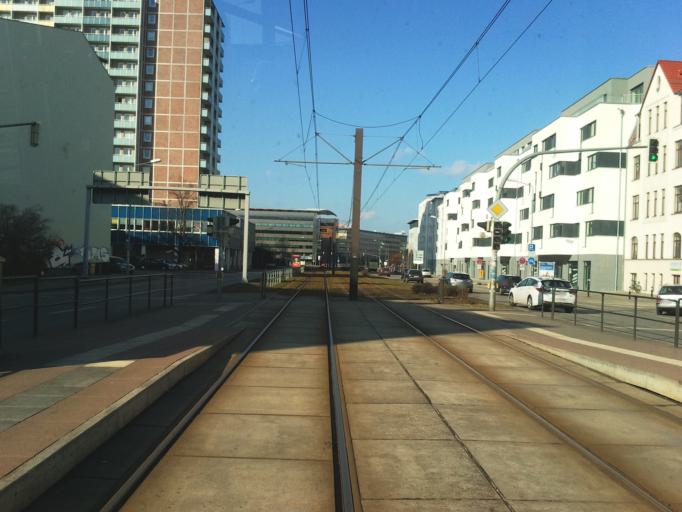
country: DE
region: Mecklenburg-Vorpommern
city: Rostock
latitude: 54.0828
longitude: 12.1272
